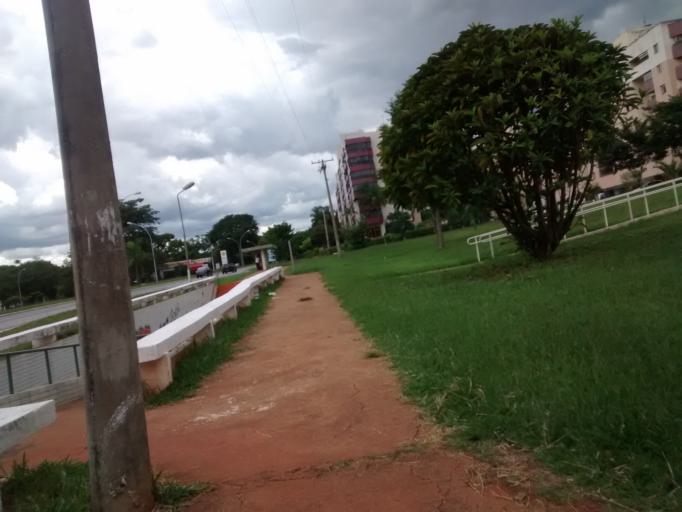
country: BR
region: Federal District
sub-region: Brasilia
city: Brasilia
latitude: -15.7589
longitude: -47.8860
